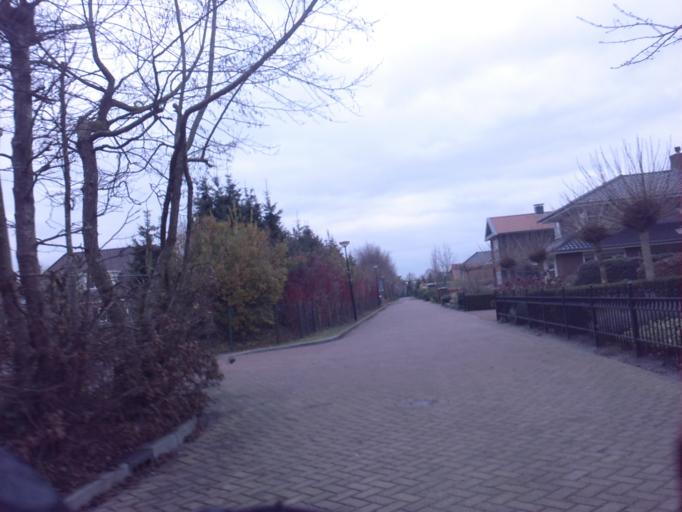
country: NL
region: Utrecht
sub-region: Gemeente Amersfoort
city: Randenbroek
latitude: 52.1846
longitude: 5.4279
